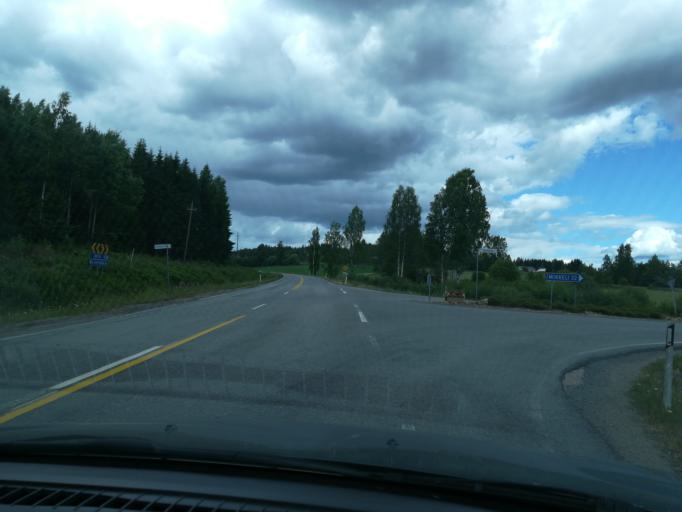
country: FI
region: Southern Savonia
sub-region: Mikkeli
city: Hirvensalmi
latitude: 61.6705
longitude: 26.7641
